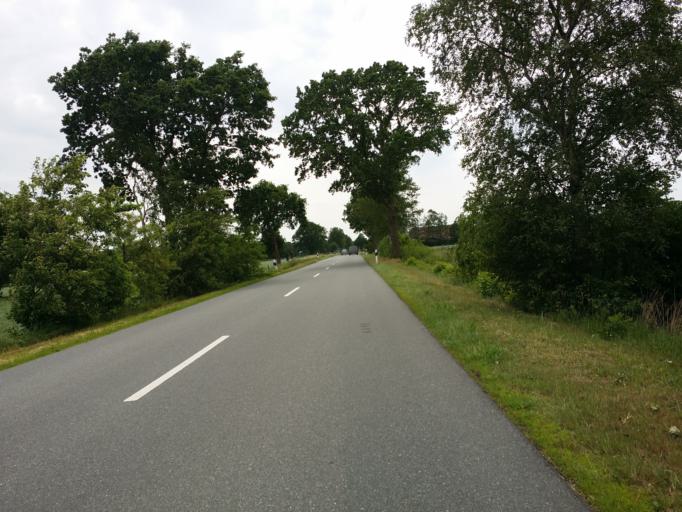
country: DE
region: Lower Saxony
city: Bockhorn
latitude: 53.3282
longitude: 8.0252
